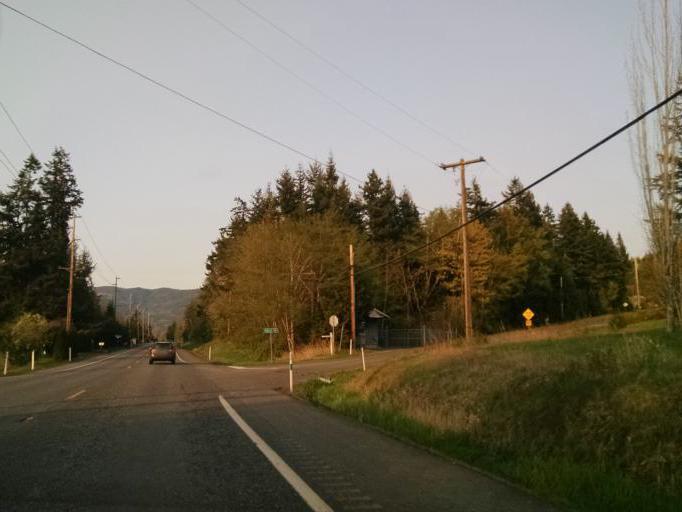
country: US
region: Washington
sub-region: Whatcom County
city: Sudden Valley
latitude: 48.8180
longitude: -122.3274
